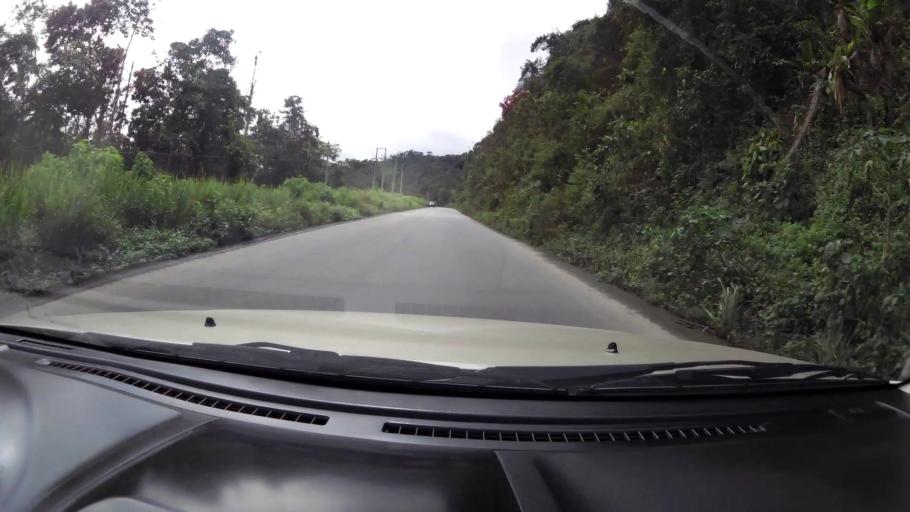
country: EC
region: El Oro
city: Pasaje
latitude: -3.3198
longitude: -79.6861
